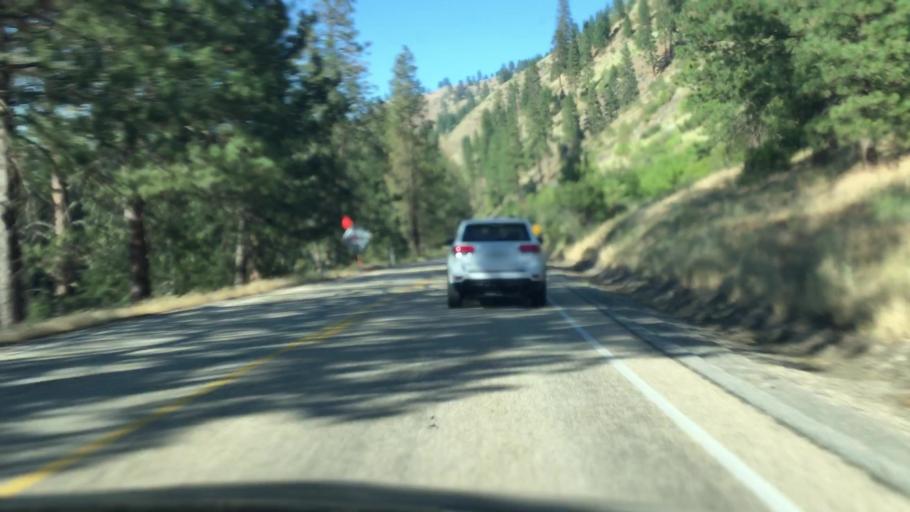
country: US
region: Idaho
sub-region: Boise County
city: Idaho City
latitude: 44.0547
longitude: -116.1305
